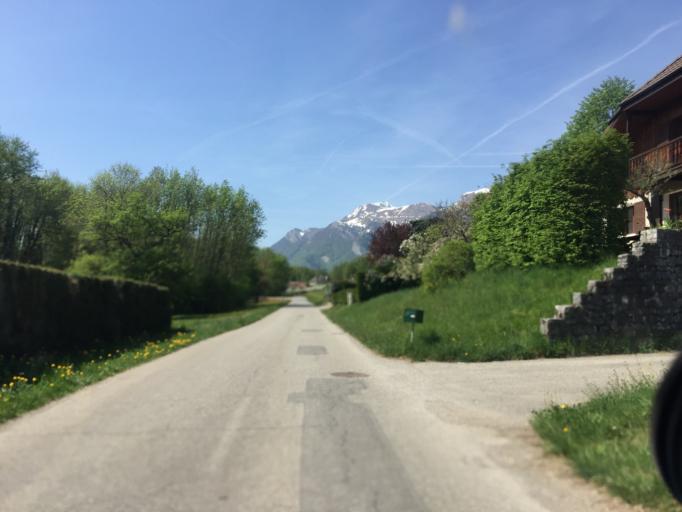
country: FR
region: Rhone-Alpes
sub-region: Departement de la Savoie
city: Mercury
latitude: 45.6732
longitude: 6.3457
